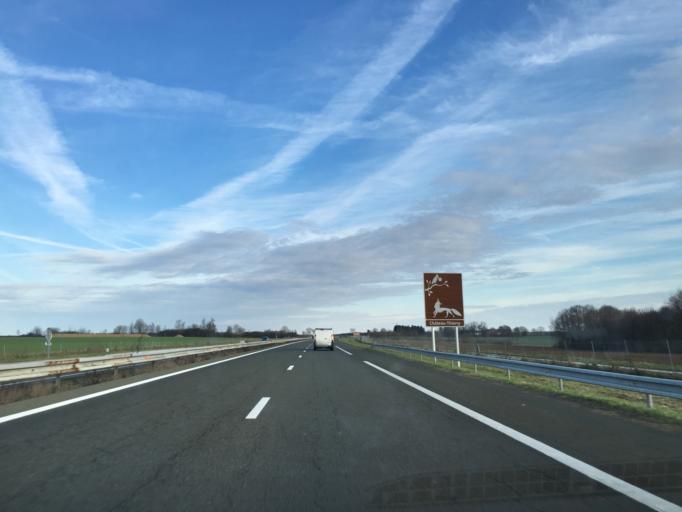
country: FR
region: Picardie
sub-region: Departement de l'Aisne
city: Essomes-sur-Marne
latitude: 49.0669
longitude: 3.3374
